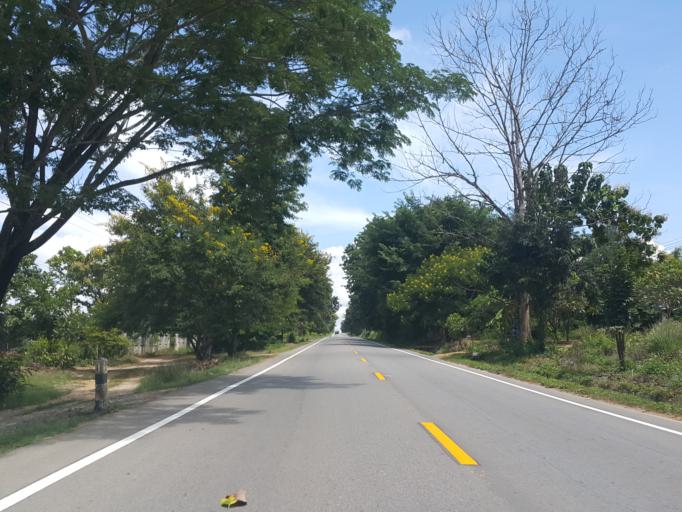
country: TH
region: Chiang Mai
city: Phrao
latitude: 19.2558
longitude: 99.1852
